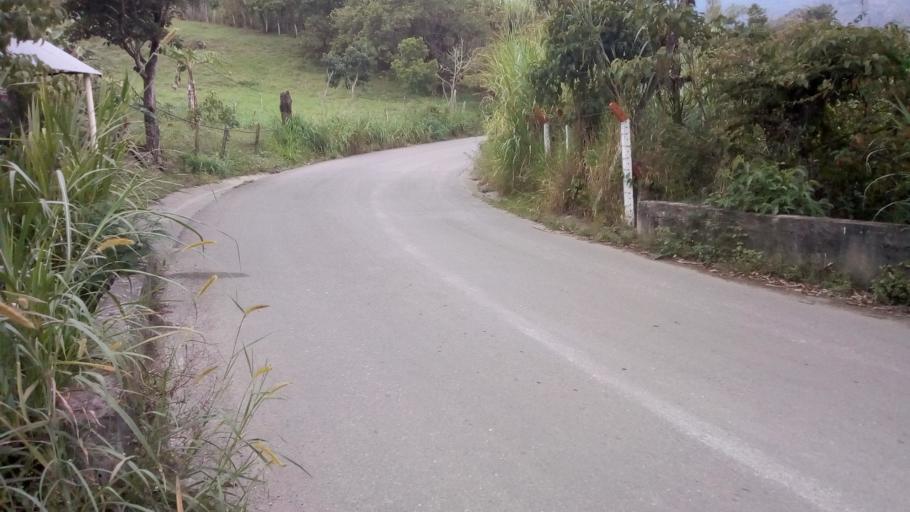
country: CO
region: Cundinamarca
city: Tenza
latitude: 5.0858
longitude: -73.4397
